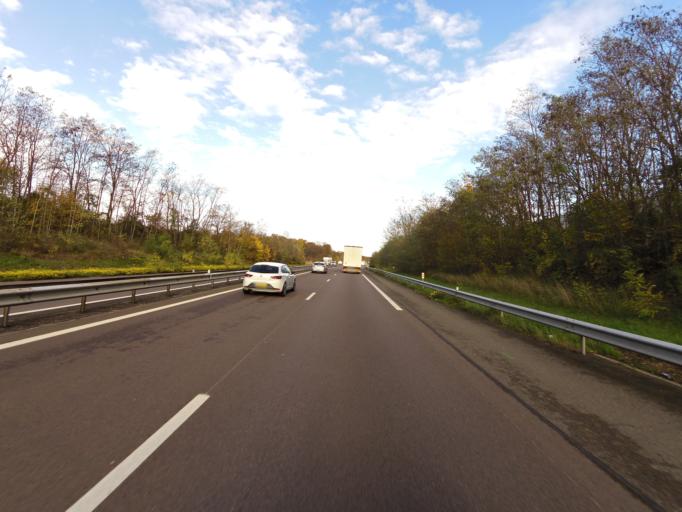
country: FR
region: Bourgogne
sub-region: Departement de la Cote-d'Or
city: Neuilly-les-Dijon
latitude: 47.2672
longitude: 5.1315
